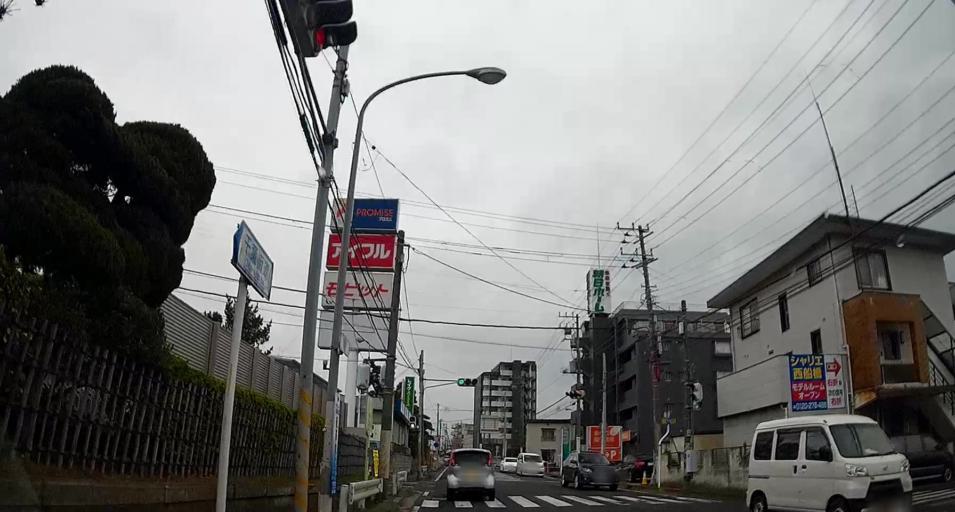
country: JP
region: Chiba
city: Funabashi
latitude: 35.7078
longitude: 139.9623
